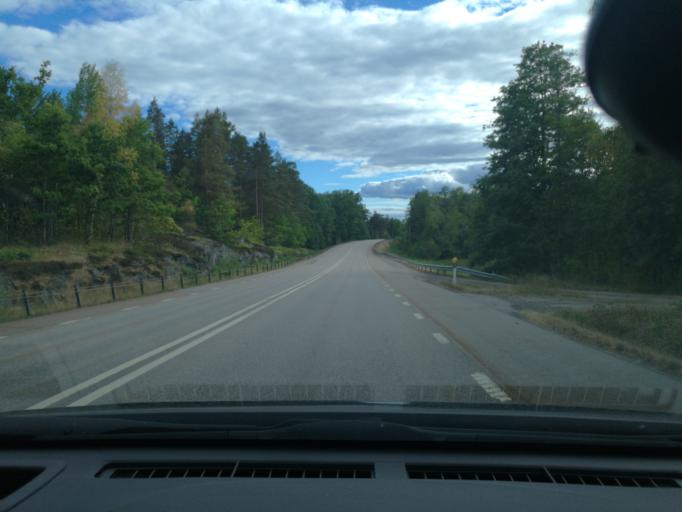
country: SE
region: Kalmar
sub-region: Oskarshamns Kommun
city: Oskarshamn
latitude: 57.4447
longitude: 16.4993
